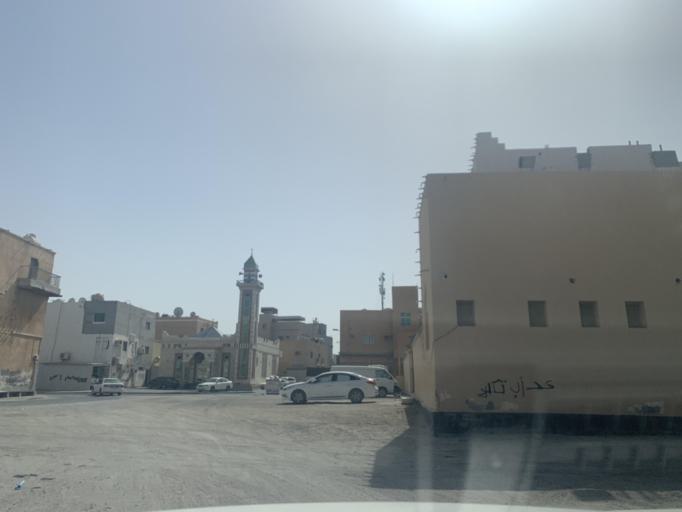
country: BH
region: Northern
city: Sitrah
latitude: 26.1693
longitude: 50.6255
